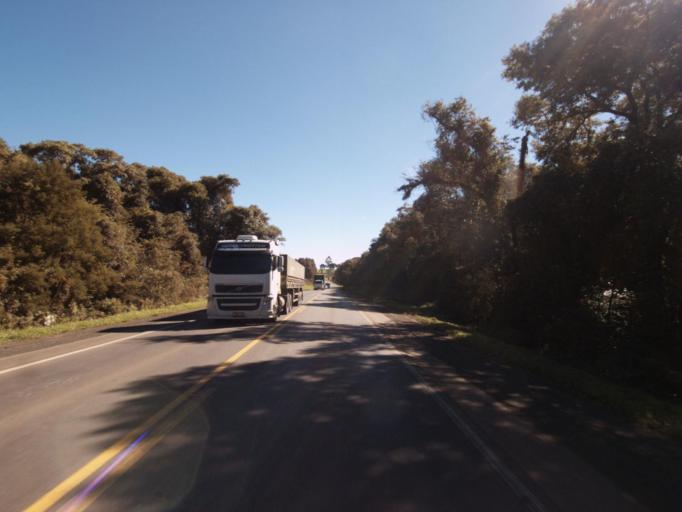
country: BR
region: Santa Catarina
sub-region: Xanxere
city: Xanxere
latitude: -26.8683
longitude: -52.2016
